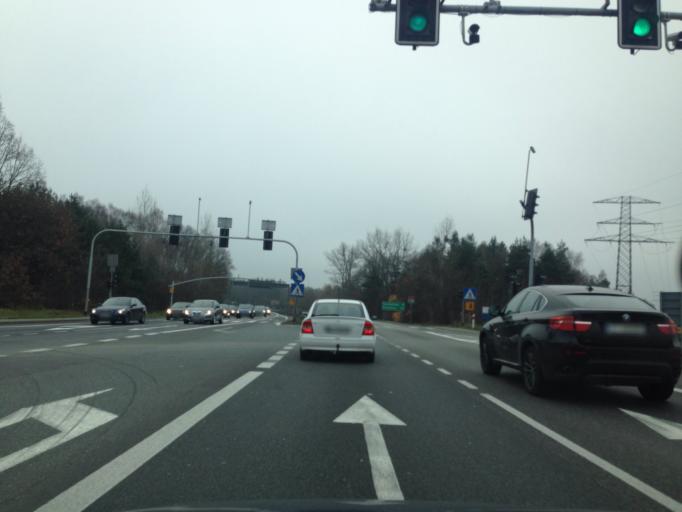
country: PL
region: Silesian Voivodeship
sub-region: Powiat czestochowski
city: Kamienica Polska
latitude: 50.6708
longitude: 19.1226
